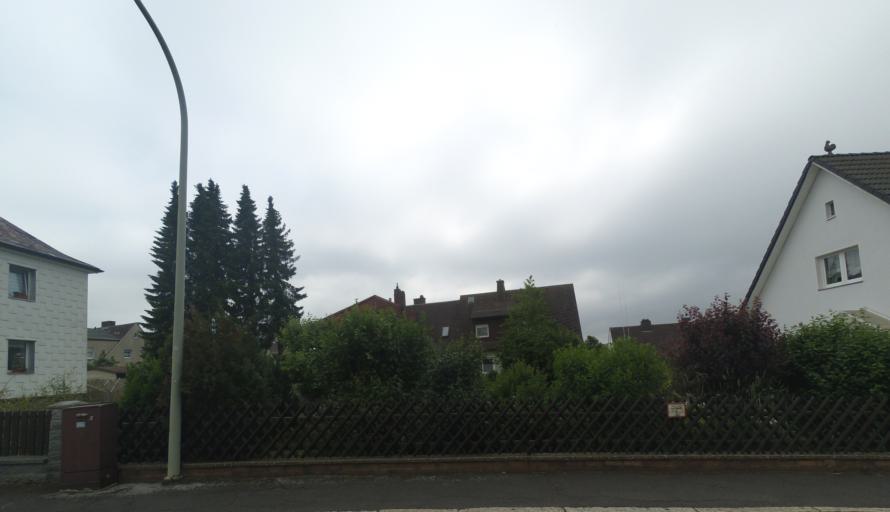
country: DE
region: Bavaria
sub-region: Upper Franconia
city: Roslau
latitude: 50.0859
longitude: 11.9669
